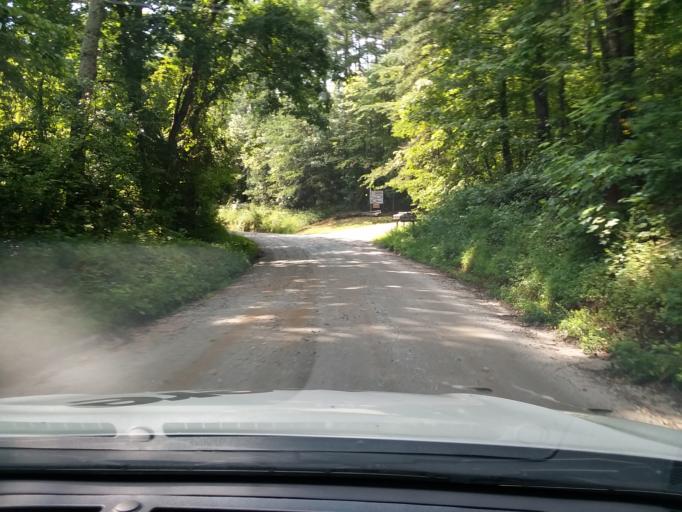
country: US
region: Georgia
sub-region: Habersham County
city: Clarkesville
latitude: 34.7200
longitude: -83.4468
